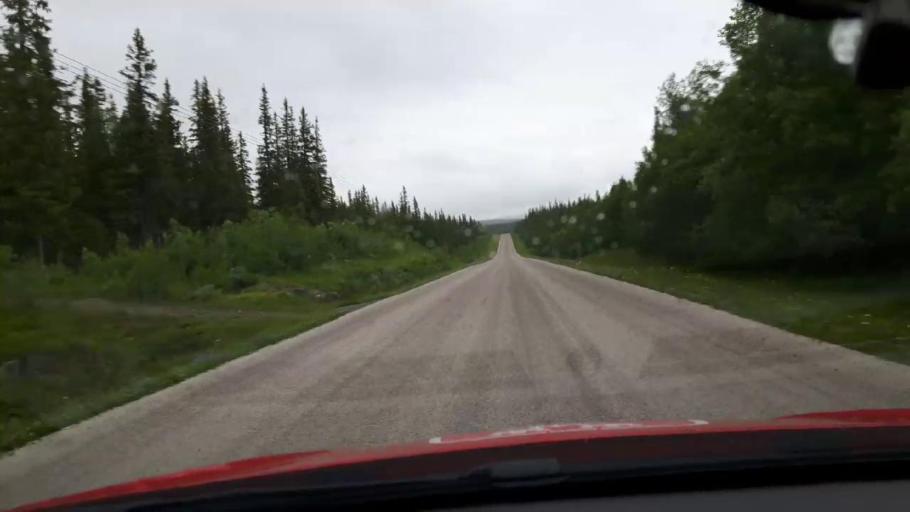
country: NO
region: Nord-Trondelag
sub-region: Meraker
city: Meraker
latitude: 63.2723
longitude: 12.3665
